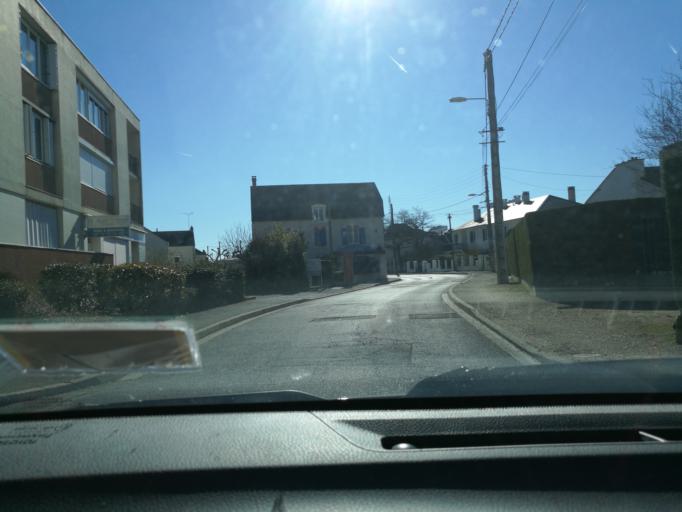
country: FR
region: Centre
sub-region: Departement du Loiret
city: Saint-Jean-le-Blanc
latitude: 47.8909
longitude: 1.9115
